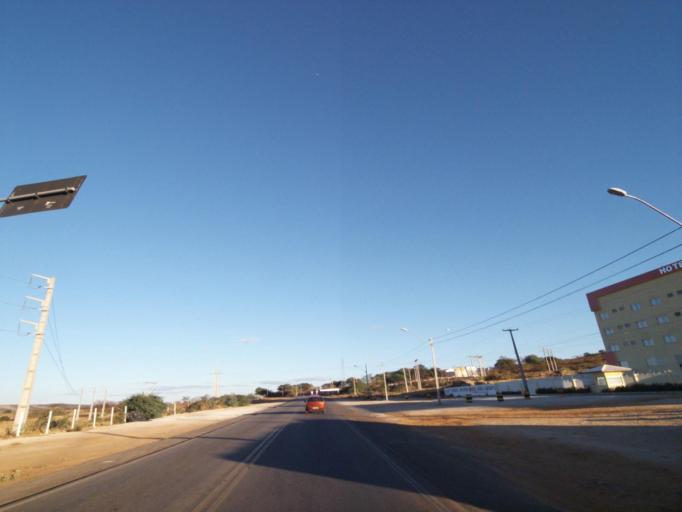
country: BR
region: Bahia
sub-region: Brumado
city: Brumado
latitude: -14.2064
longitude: -41.6537
